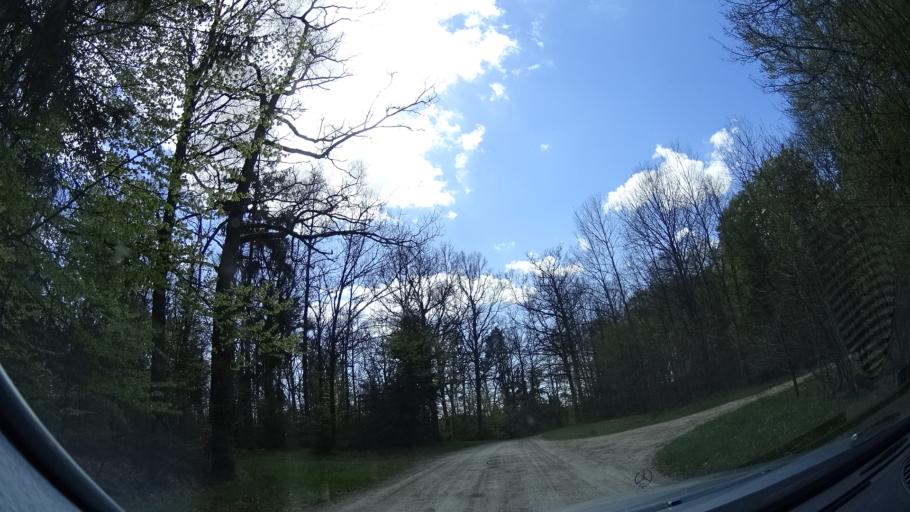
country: SE
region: Skane
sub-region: Hassleholms Kommun
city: Tormestorp
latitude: 56.0898
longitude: 13.7119
